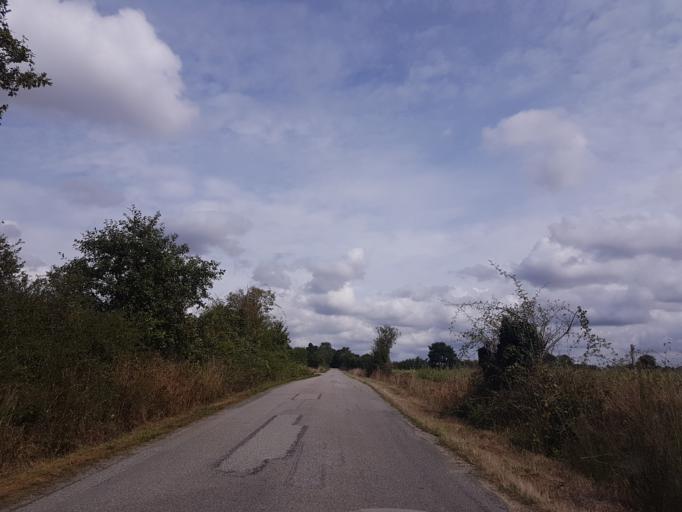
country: FR
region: Pays de la Loire
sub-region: Departement de la Loire-Atlantique
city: Petit-Mars
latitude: 47.3915
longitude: -1.4311
